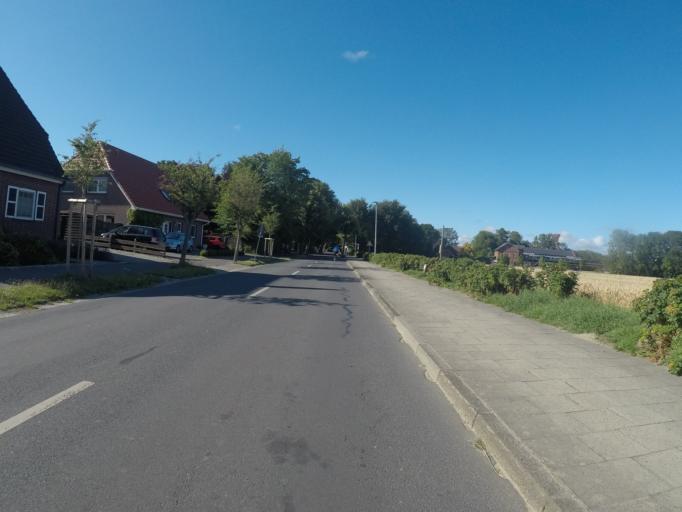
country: DE
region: Lower Saxony
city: Otterndorf
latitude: 53.8206
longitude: 8.8962
